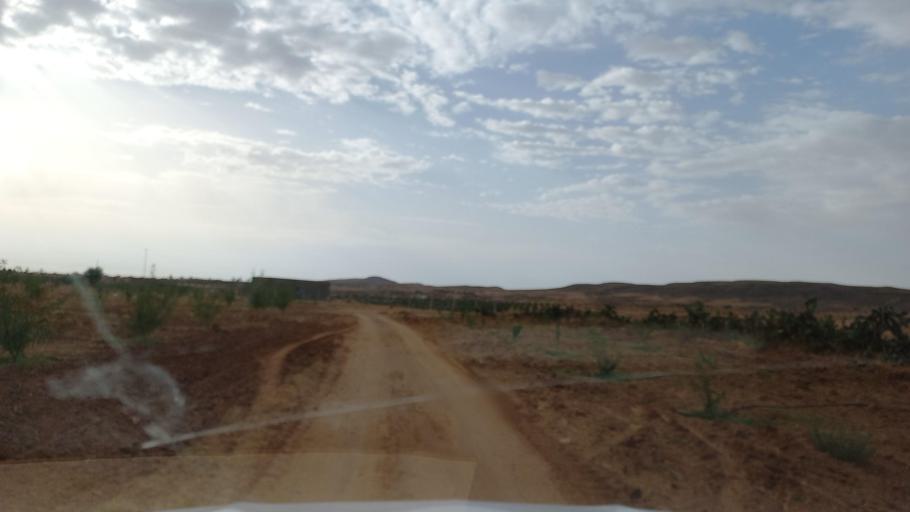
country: TN
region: Al Qasrayn
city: Kasserine
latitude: 35.1888
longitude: 9.0525
